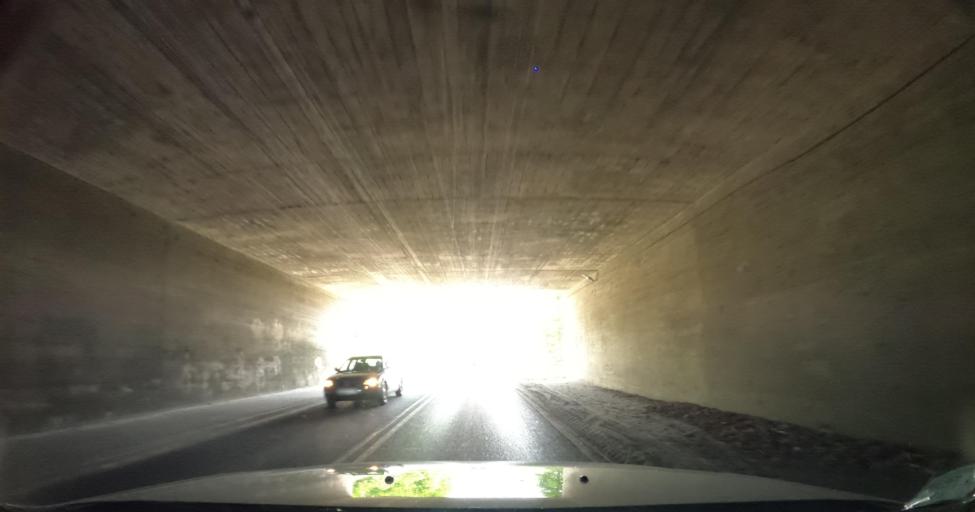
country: PL
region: Warmian-Masurian Voivodeship
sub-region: Powiat lidzbarski
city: Lidzbark Warminski
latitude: 54.1309
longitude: 20.5654
